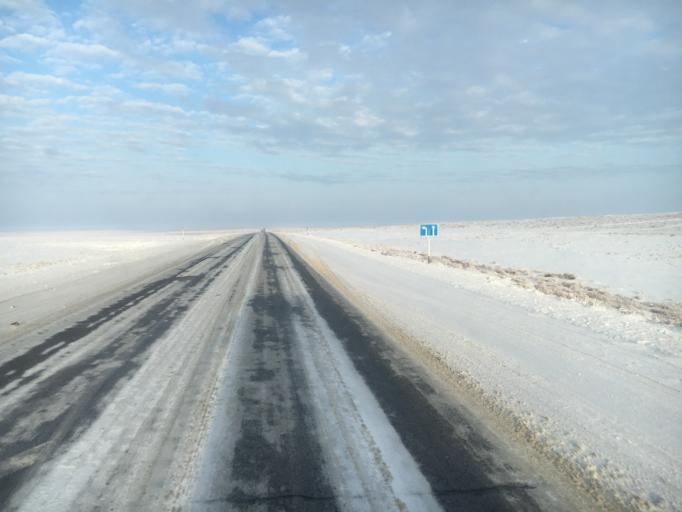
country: KZ
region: Qyzylorda
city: Sekseuil
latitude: 47.7163
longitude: 61.3971
